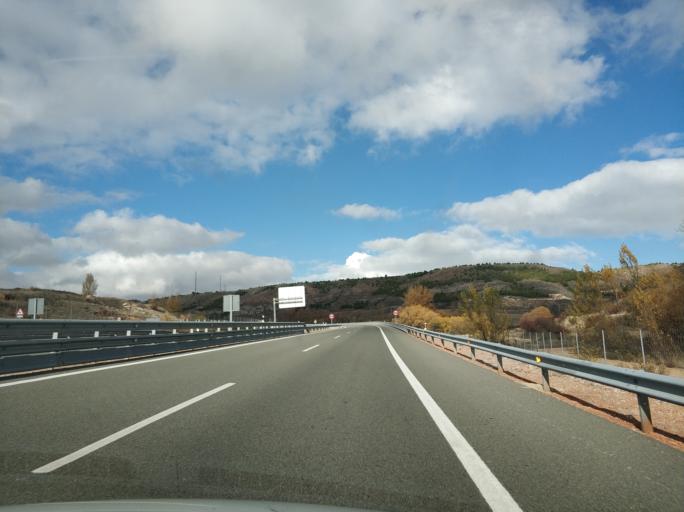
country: ES
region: Castille and Leon
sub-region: Provincia de Soria
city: Medinaceli
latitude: 41.1863
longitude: -2.4310
